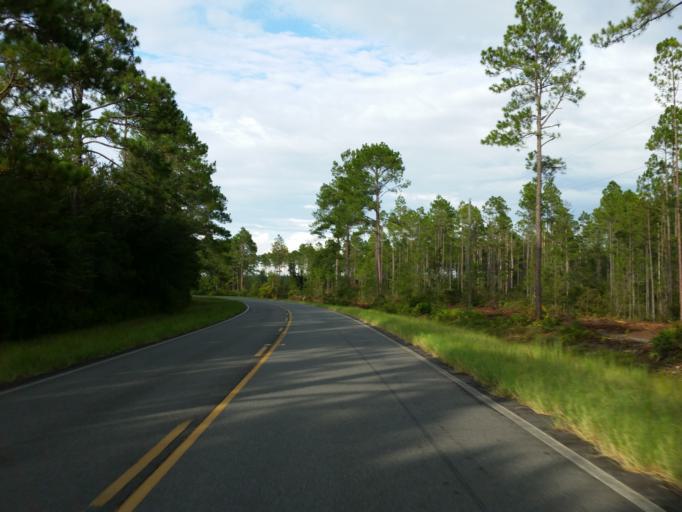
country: US
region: Florida
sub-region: Hamilton County
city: Jasper
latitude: 30.6386
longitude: -82.5814
